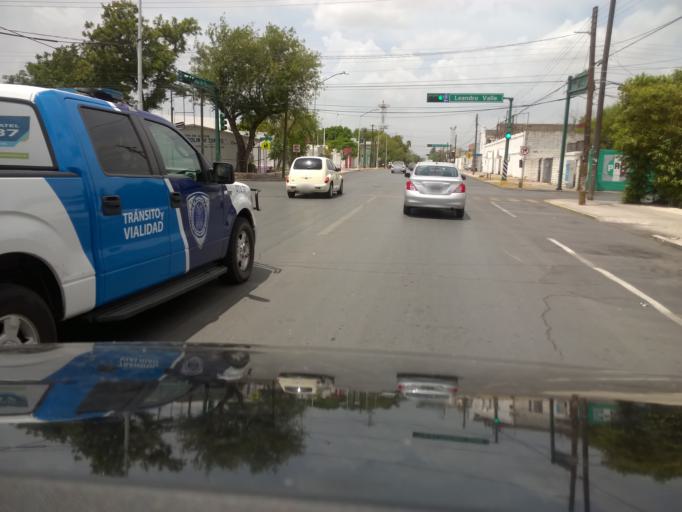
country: MX
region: Tamaulipas
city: Nuevo Laredo
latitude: 27.4867
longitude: -99.5027
